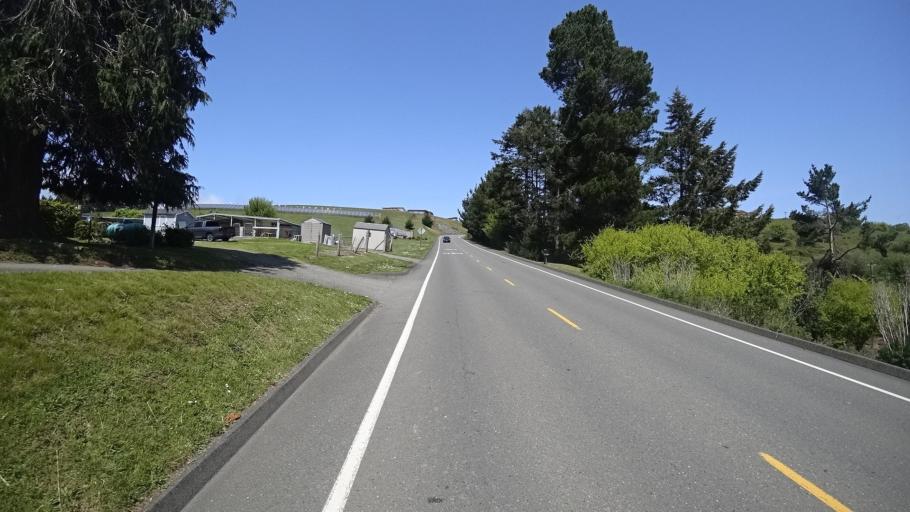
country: US
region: California
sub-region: Humboldt County
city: Fortuna
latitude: 40.6233
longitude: -124.2115
